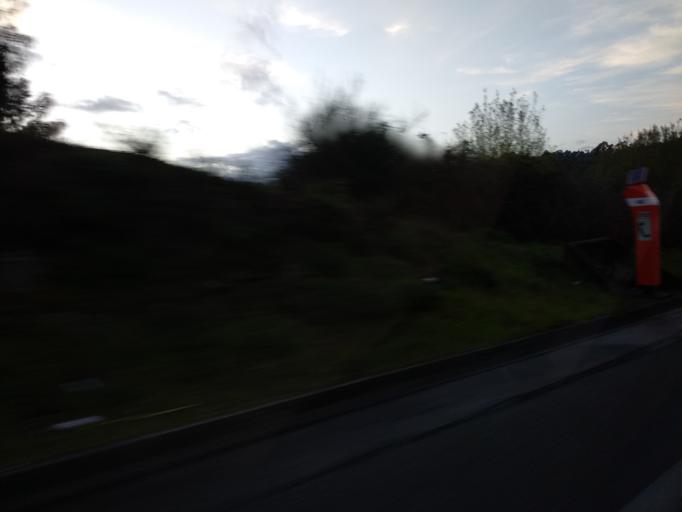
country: PT
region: Braga
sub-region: Braga
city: Oliveira
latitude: 41.4789
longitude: -8.4591
